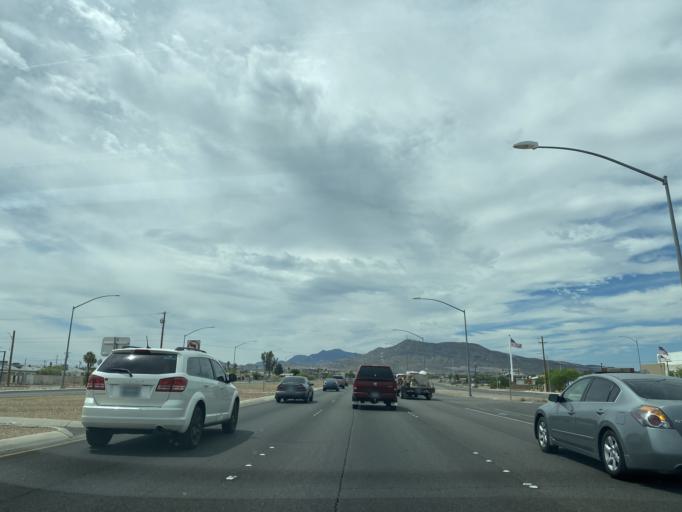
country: US
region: Nevada
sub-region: Clark County
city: Henderson
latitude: 36.0497
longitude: -114.9717
